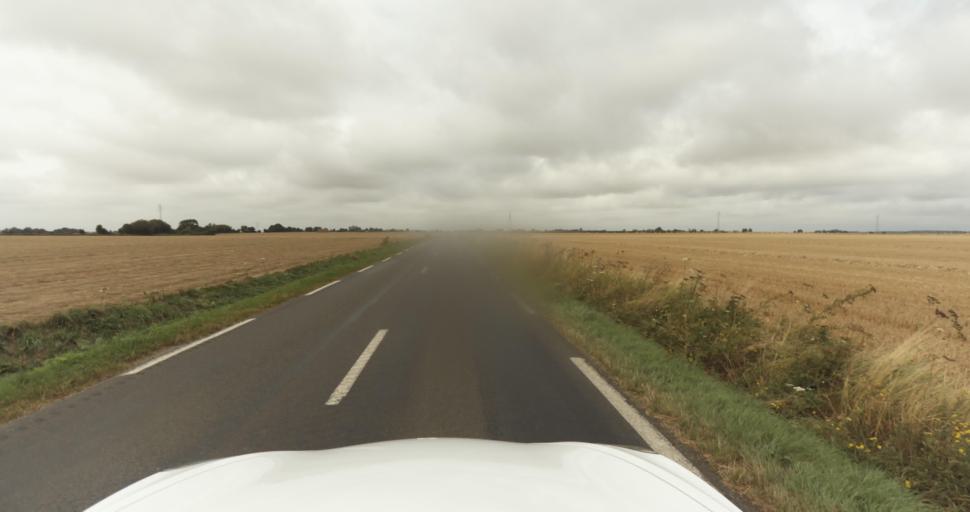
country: FR
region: Haute-Normandie
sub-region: Departement de l'Eure
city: Claville
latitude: 49.0794
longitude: 1.0573
